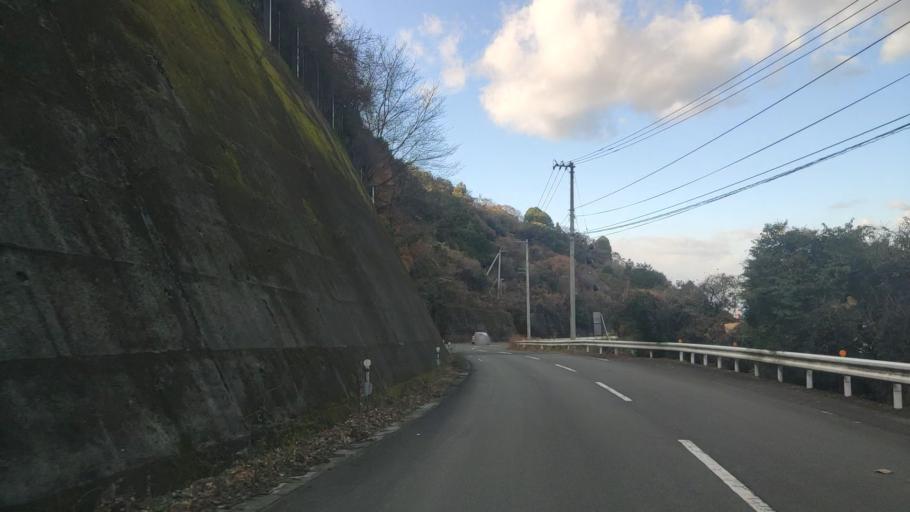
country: JP
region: Ehime
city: Saijo
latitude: 33.8800
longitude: 133.1332
